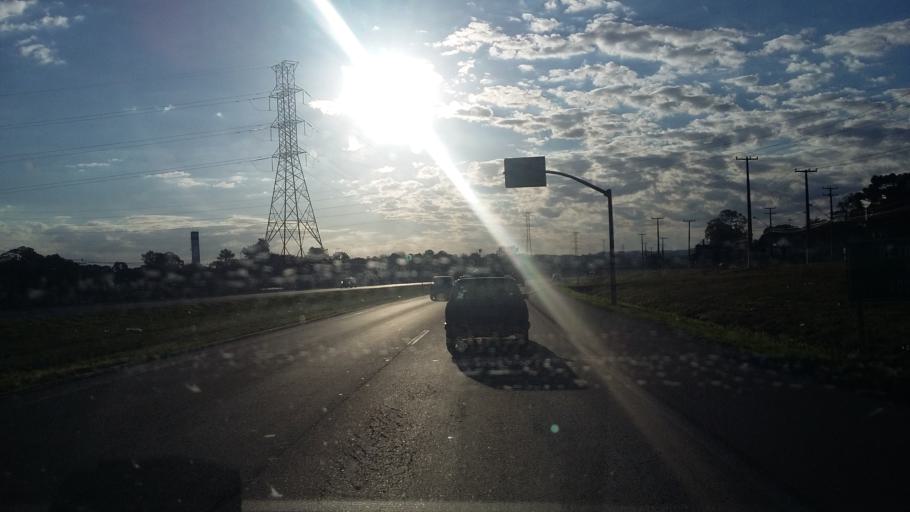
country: BR
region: Parana
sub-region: Araucaria
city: Araucaria
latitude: -25.5300
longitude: -49.3258
